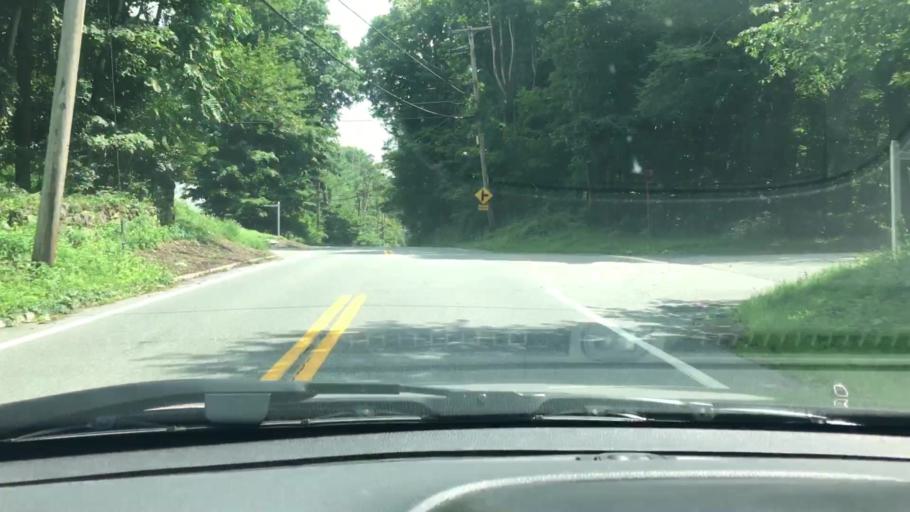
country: US
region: New York
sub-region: Westchester County
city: Pound Ridge
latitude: 41.1643
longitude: -73.5999
